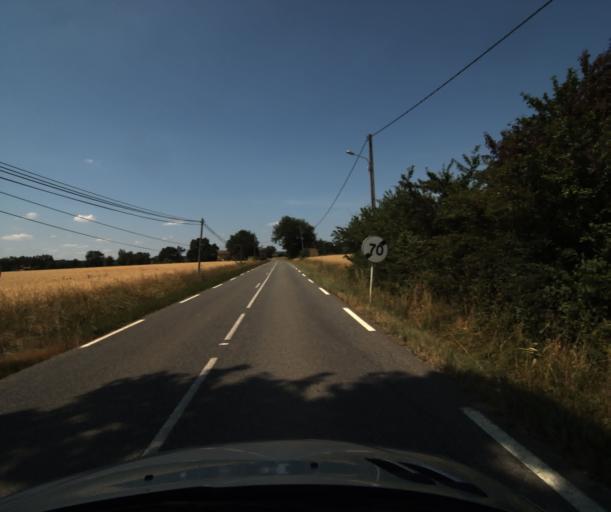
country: FR
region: Midi-Pyrenees
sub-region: Departement de la Haute-Garonne
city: Saint-Lys
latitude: 43.5263
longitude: 1.1723
